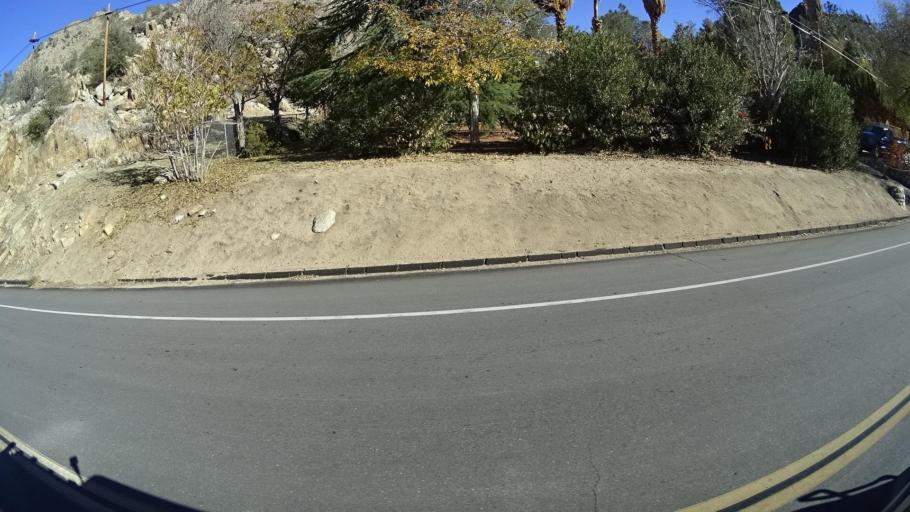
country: US
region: California
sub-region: Kern County
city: Kernville
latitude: 35.7405
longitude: -118.4147
